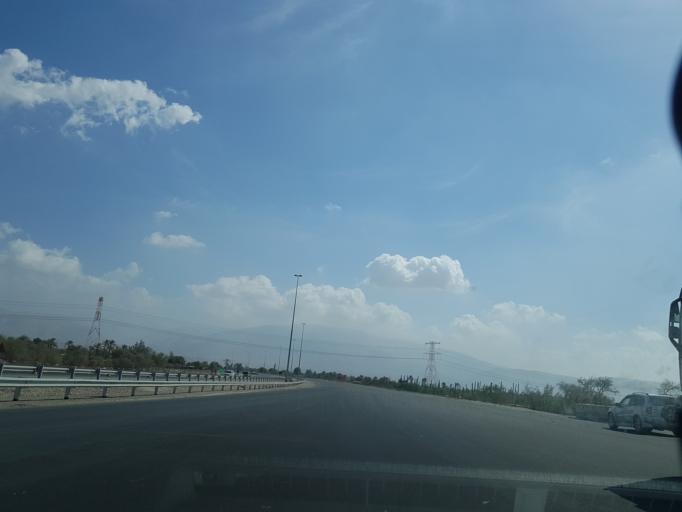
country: AE
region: Ra's al Khaymah
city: Ras al-Khaimah
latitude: 25.6978
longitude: 55.9744
